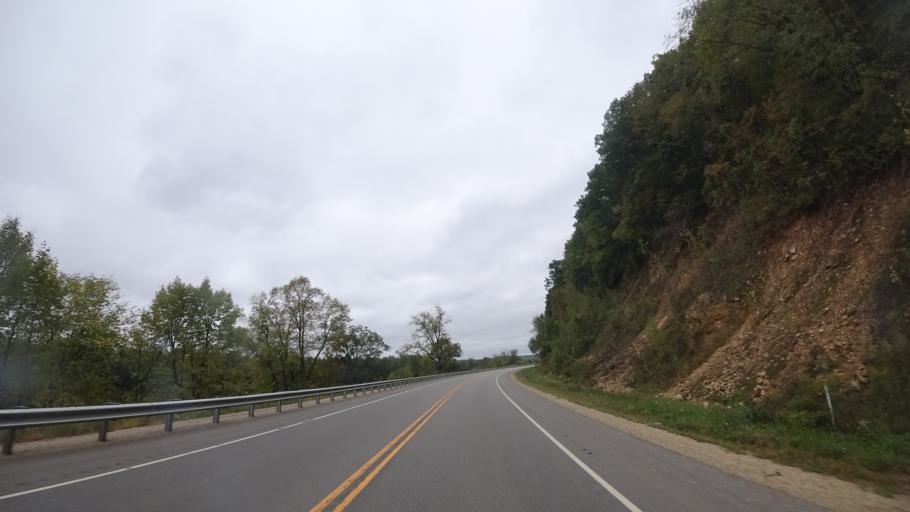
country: US
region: Wisconsin
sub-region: Grant County
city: Boscobel
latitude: 43.1644
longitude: -90.7052
